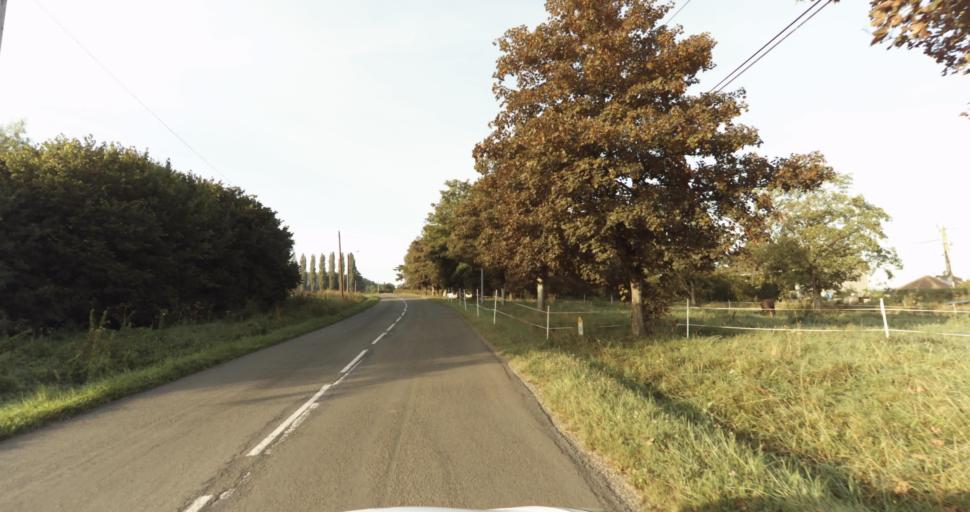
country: FR
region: Champagne-Ardenne
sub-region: Departement des Ardennes
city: Villers-Semeuse
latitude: 49.7340
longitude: 4.7412
